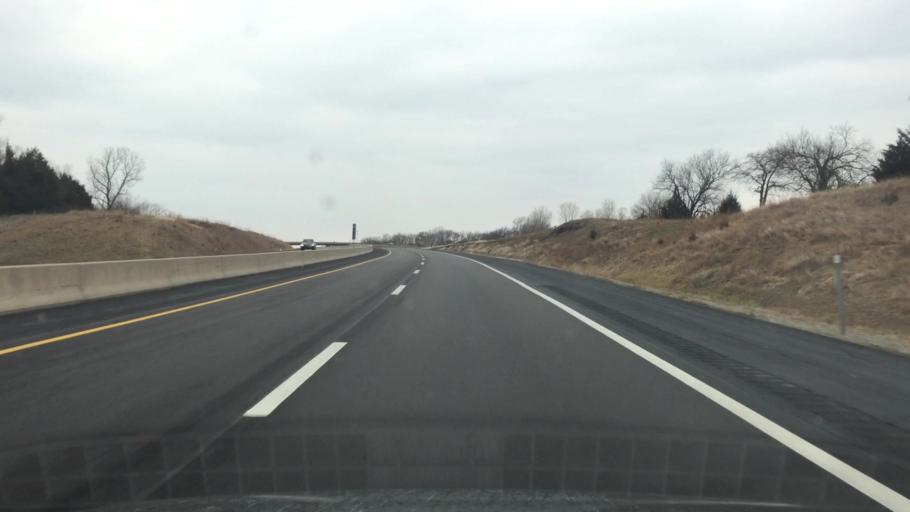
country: US
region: Kansas
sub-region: Shawnee County
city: Auburn
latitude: 38.8908
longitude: -95.8117
